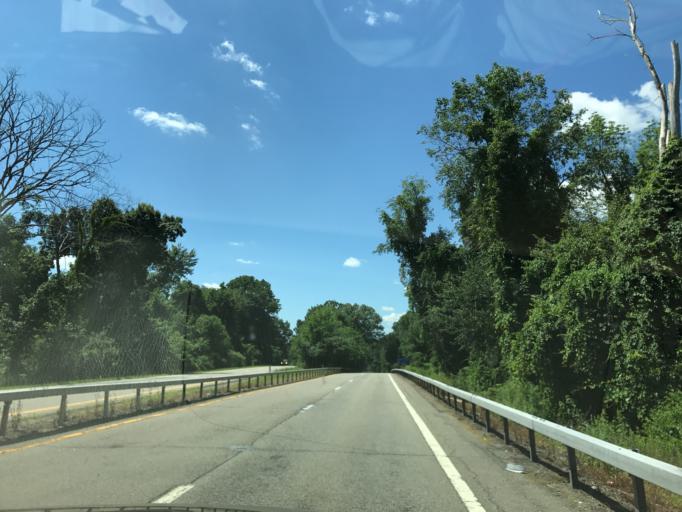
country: US
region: New York
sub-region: Dutchess County
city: Hillside Lake
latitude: 41.5695
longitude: -73.7808
